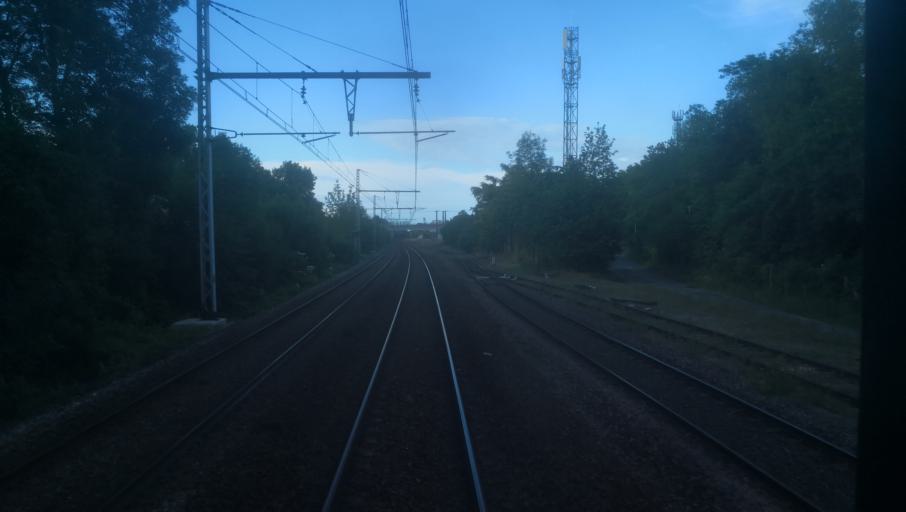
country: FR
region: Centre
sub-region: Departement de l'Indre
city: Issoudun
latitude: 46.9600
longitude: 1.9936
